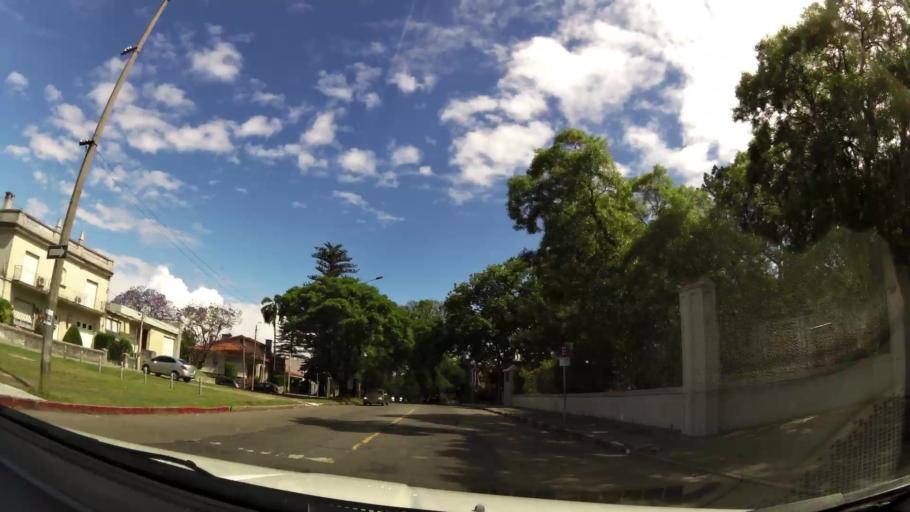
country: UY
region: Montevideo
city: Montevideo
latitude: -34.8606
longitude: -56.1966
